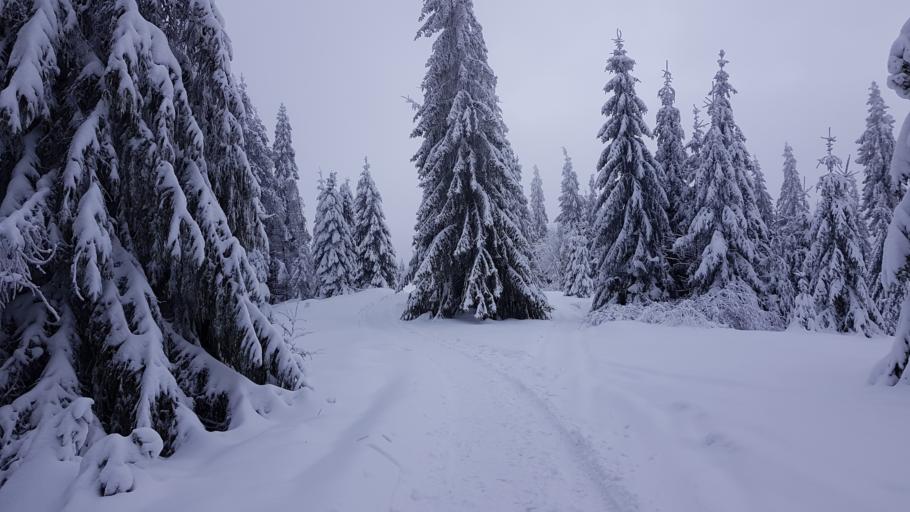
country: PL
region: Lesser Poland Voivodeship
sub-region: Powiat limanowski
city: Niedzwiedz
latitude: 49.5594
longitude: 20.0749
